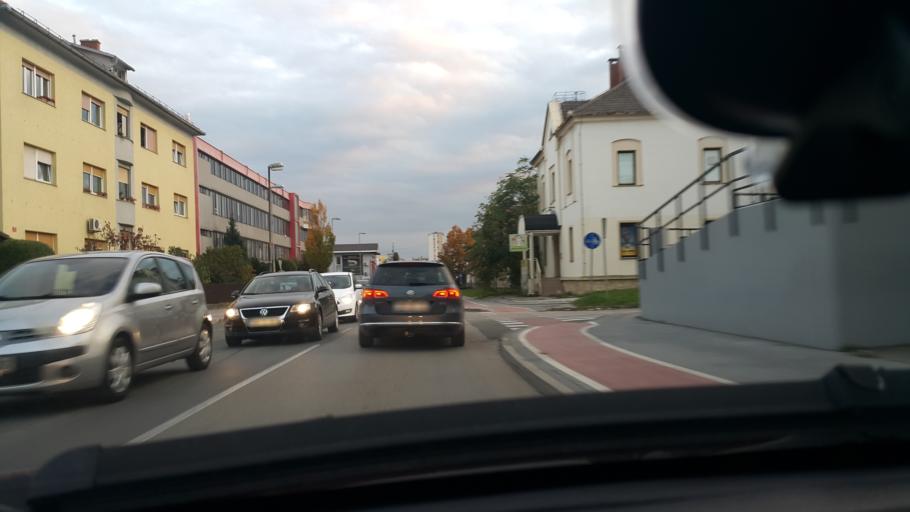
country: SI
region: Maribor
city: Maribor
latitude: 46.5605
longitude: 15.6640
